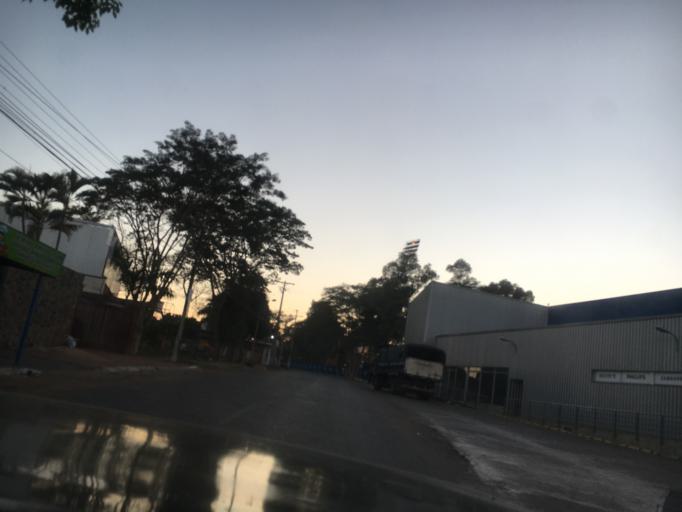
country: PY
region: Central
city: Villa Elisa
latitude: -25.3673
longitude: -57.5866
